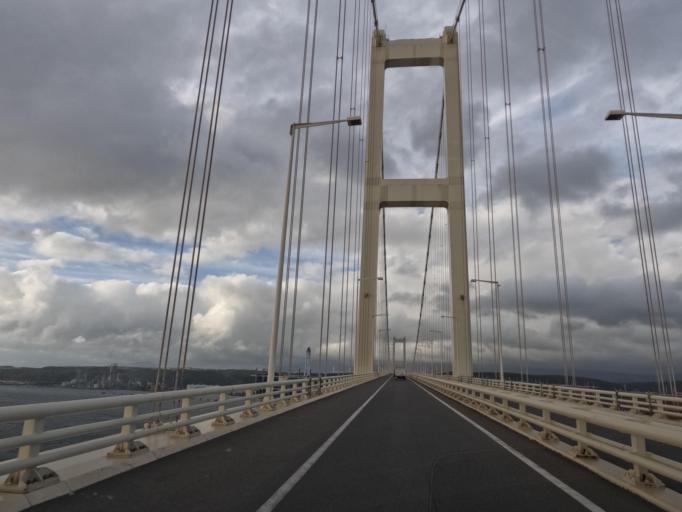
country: JP
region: Hokkaido
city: Muroran
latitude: 42.3495
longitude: 140.9494
